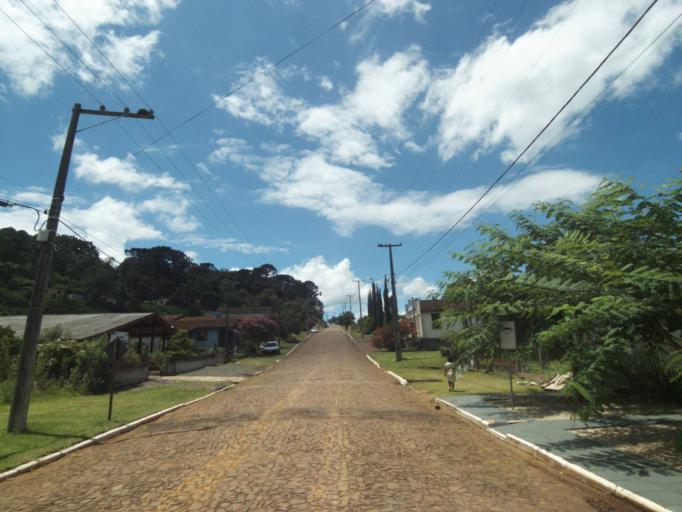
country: BR
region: Parana
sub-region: Uniao Da Vitoria
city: Uniao da Vitoria
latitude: -26.1671
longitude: -51.5574
